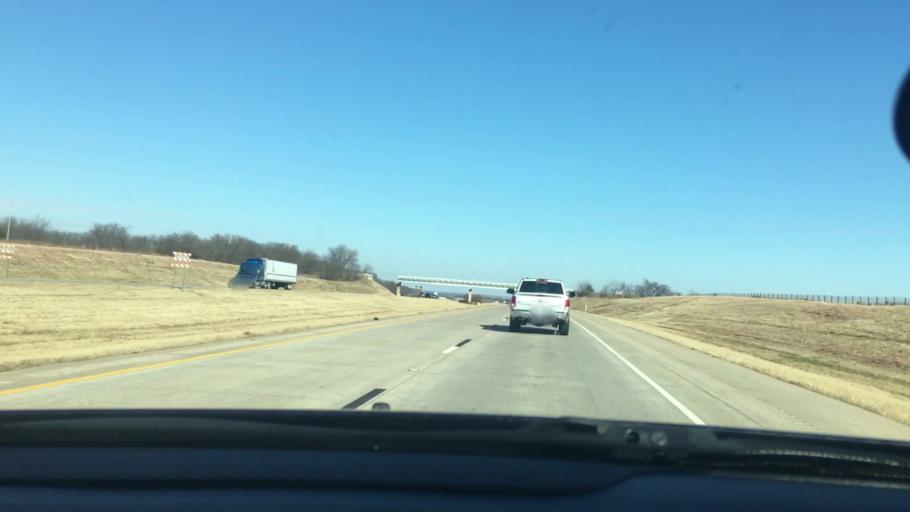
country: US
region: Oklahoma
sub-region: Love County
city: Marietta
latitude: 33.9591
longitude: -97.1341
